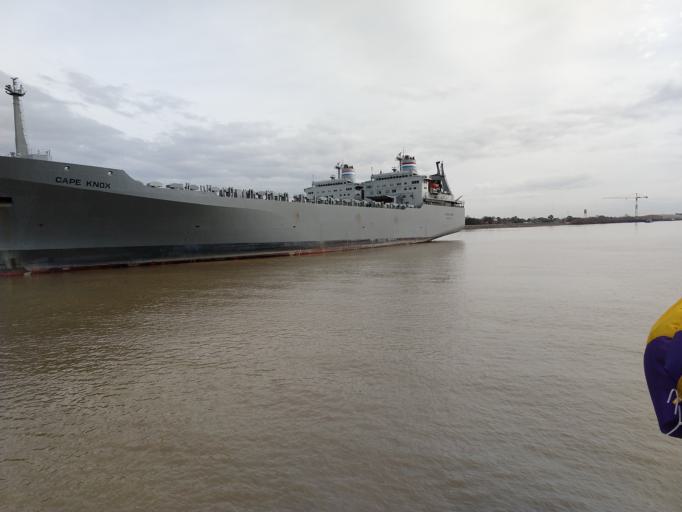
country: US
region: Louisiana
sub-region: Saint Bernard Parish
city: Arabi
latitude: 29.9572
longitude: -90.0345
